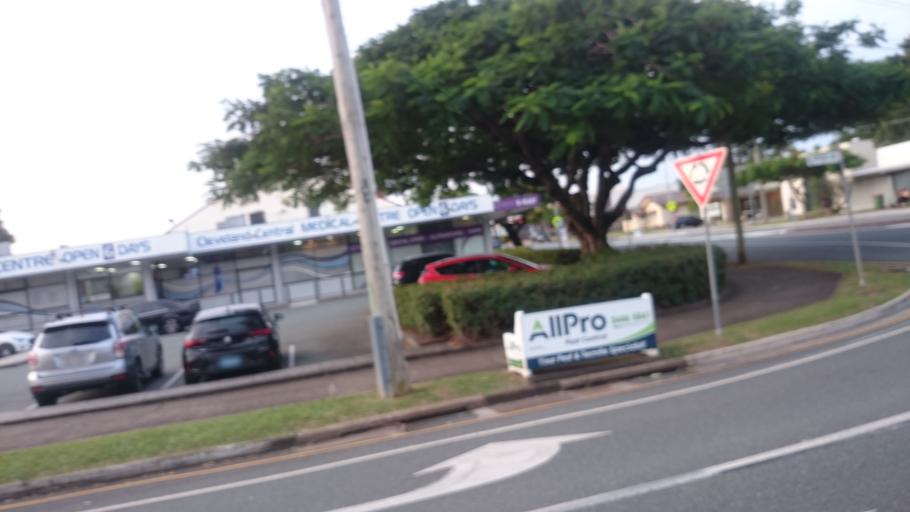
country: AU
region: Queensland
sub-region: Redland
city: Cleveland
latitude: -27.5300
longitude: 153.2666
